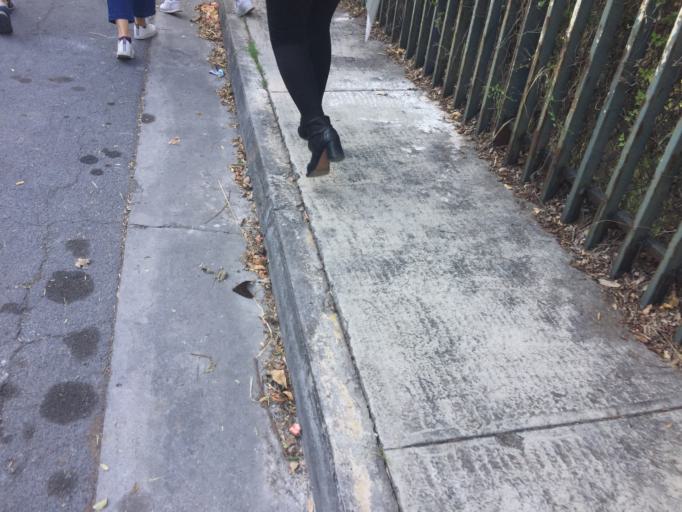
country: MX
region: Nuevo Leon
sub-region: San Pedro Garza Garcia
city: San Pedro Garza Garcia
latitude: 25.6568
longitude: -100.3976
